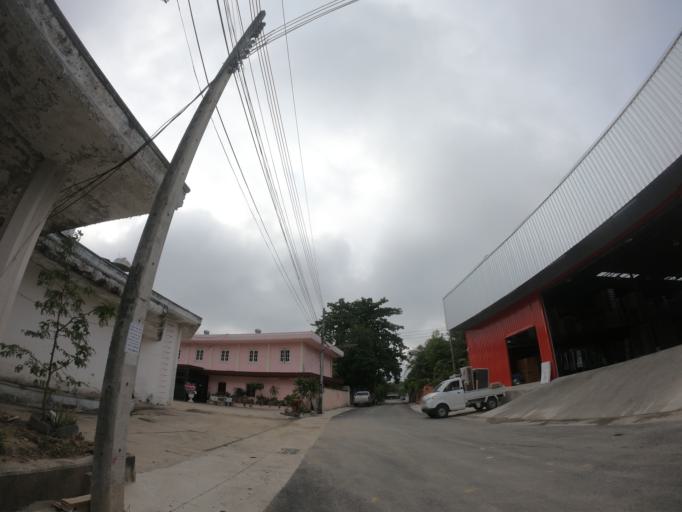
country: TH
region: Chiang Mai
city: Chiang Mai
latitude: 18.7716
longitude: 98.9810
